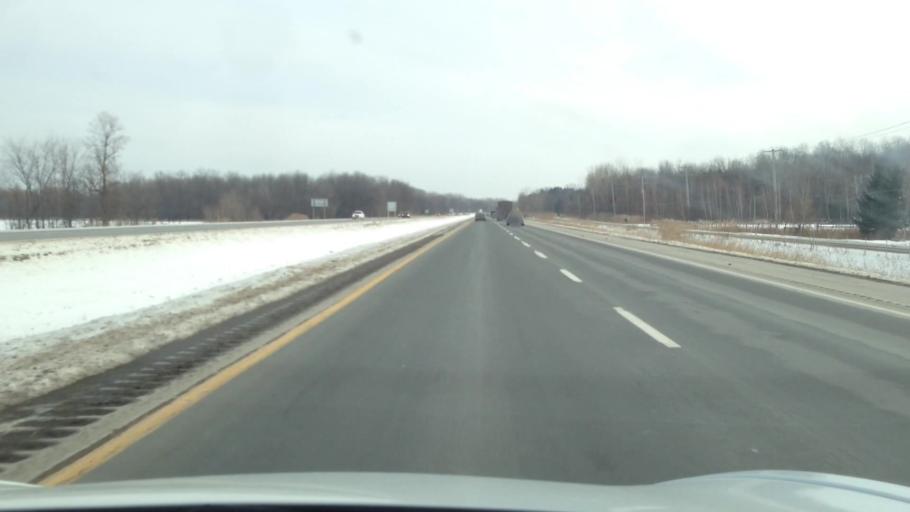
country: CA
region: Quebec
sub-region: Monteregie
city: Rigaud
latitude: 45.4724
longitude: -74.2671
